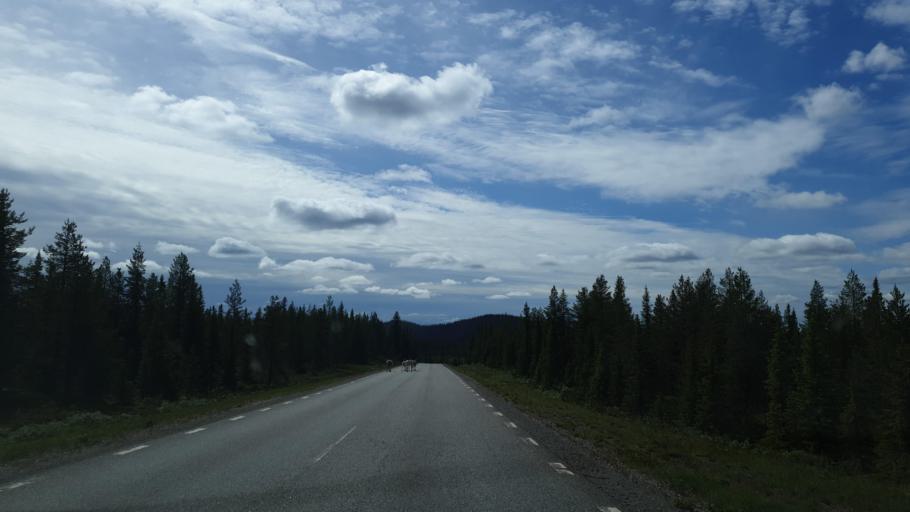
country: SE
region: Vaesterbotten
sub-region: Mala Kommun
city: Mala
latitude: 65.5774
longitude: 18.4349
